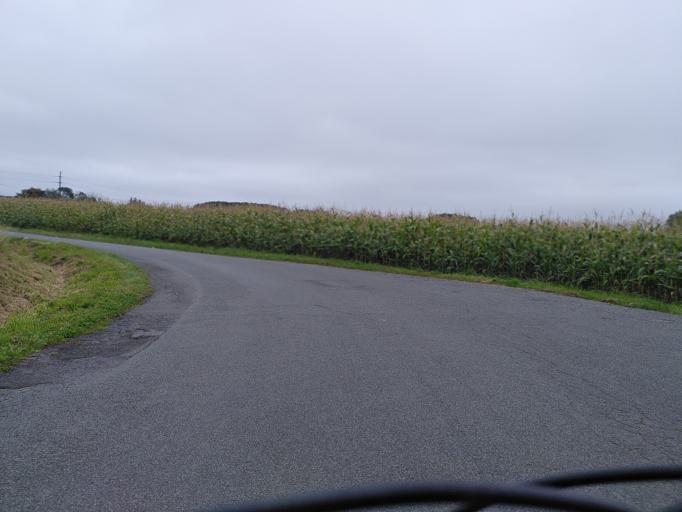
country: FR
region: Nord-Pas-de-Calais
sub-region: Departement du Pas-de-Calais
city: Isbergues
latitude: 50.6302
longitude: 2.4648
